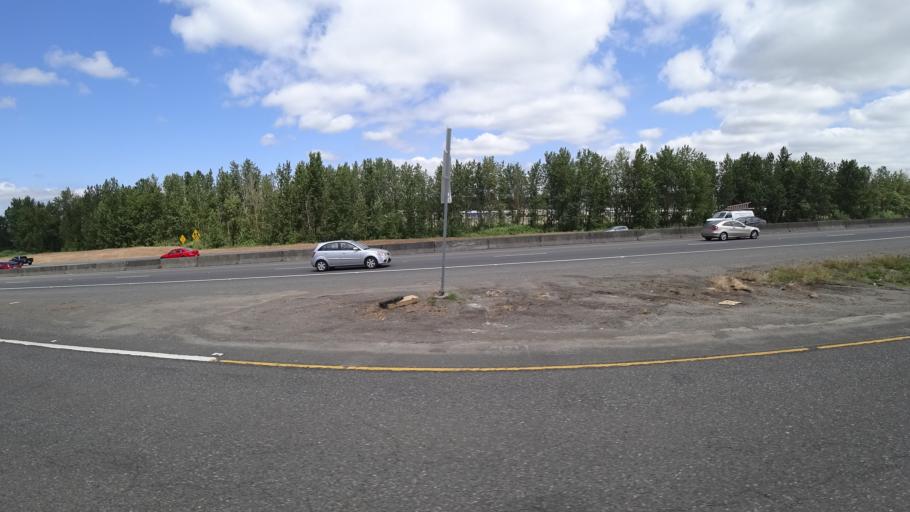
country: US
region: Washington
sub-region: Clark County
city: Vancouver
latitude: 45.6182
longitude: -122.6560
